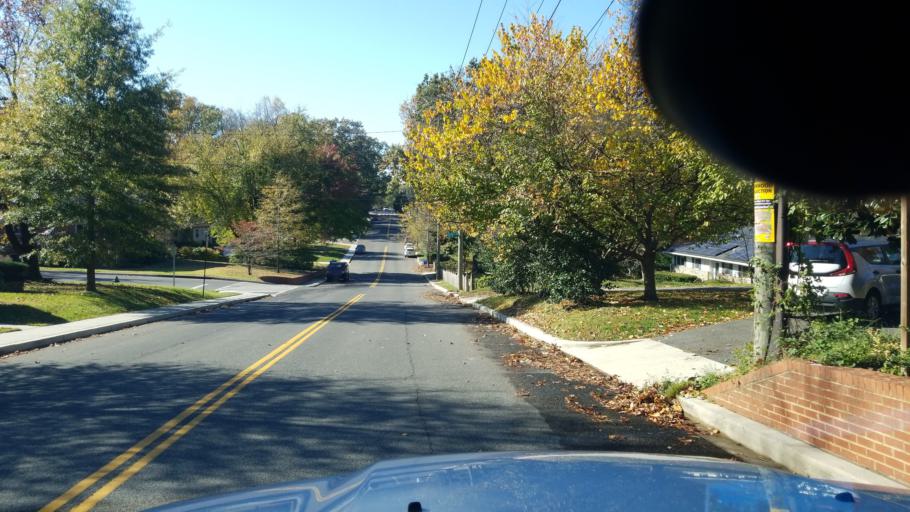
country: US
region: Maryland
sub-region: Montgomery County
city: Chevy Chase
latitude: 38.9845
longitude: -77.0554
